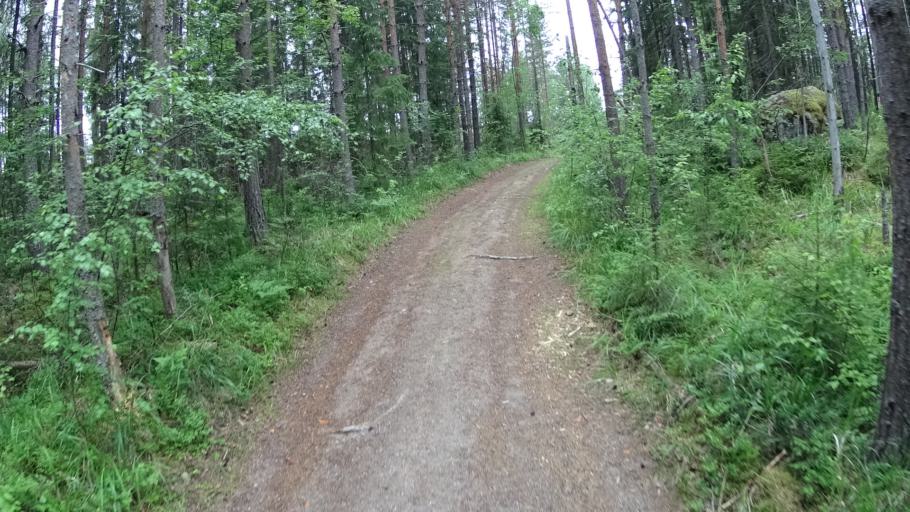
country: FI
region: Southern Savonia
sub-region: Mikkeli
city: Maentyharju
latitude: 61.1841
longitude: 26.8264
